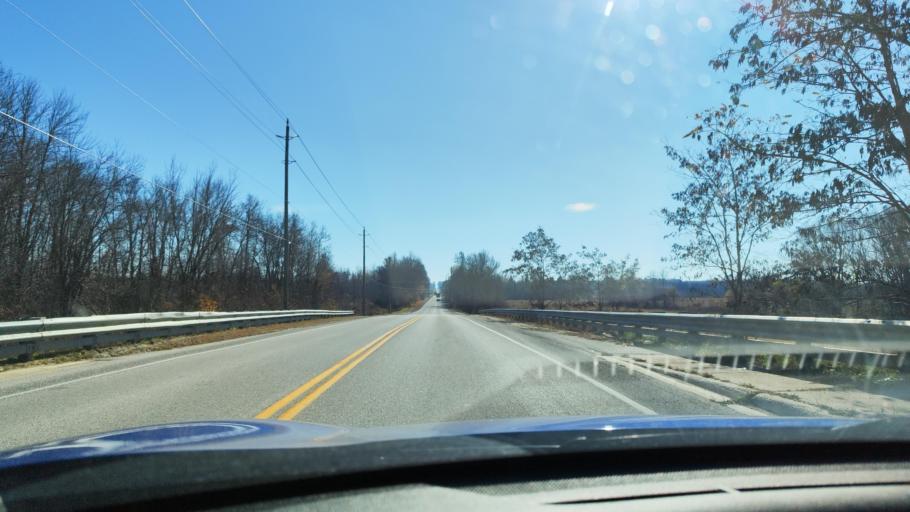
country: CA
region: Ontario
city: Wasaga Beach
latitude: 44.4751
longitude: -80.0071
